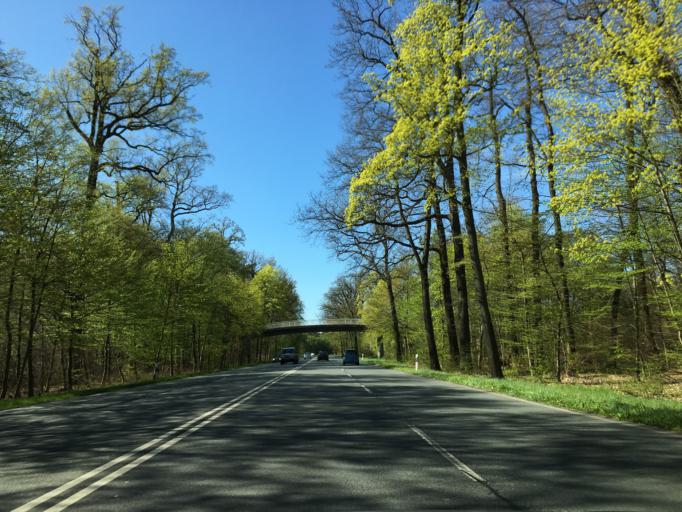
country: DE
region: Hesse
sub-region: Regierungsbezirk Darmstadt
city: Offenbach
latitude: 50.0738
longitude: 8.7374
